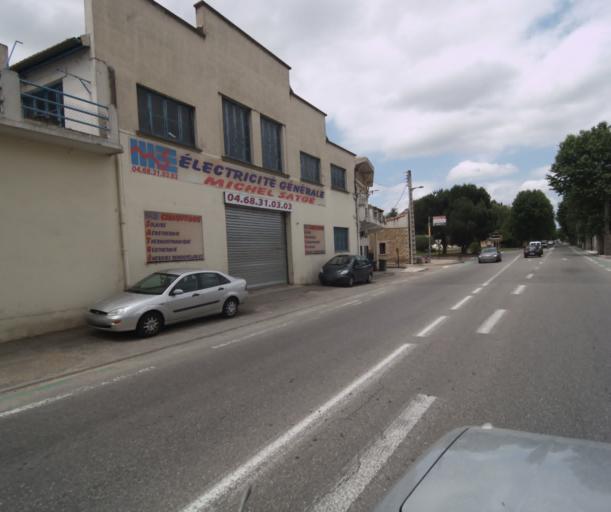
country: FR
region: Languedoc-Roussillon
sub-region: Departement de l'Aude
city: Limoux
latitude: 43.0614
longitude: 2.2147
